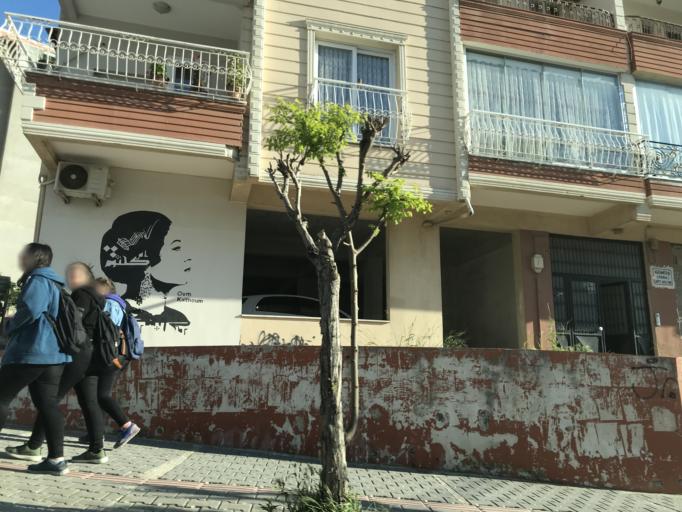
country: TR
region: Hatay
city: Samandag
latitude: 36.0874
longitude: 35.9704
